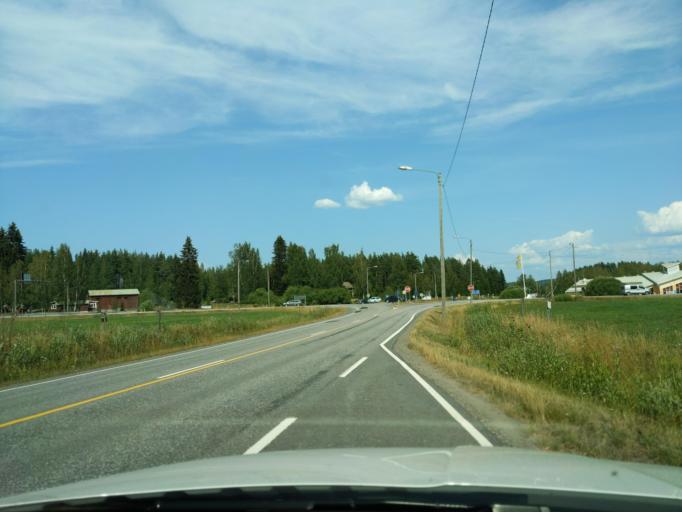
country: FI
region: Paijanne Tavastia
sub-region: Lahti
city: Padasjoki
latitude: 61.3426
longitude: 25.2465
